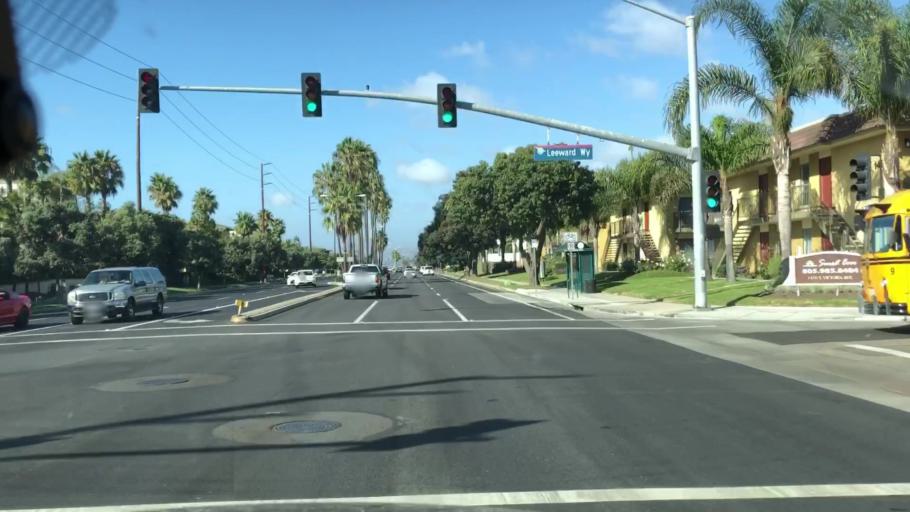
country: US
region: California
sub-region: Ventura County
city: Oxnard Shores
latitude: 34.1855
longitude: -119.2213
